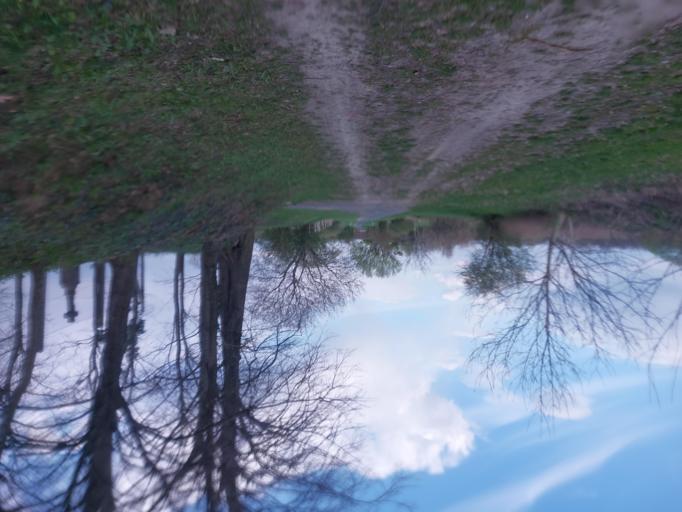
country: HU
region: Veszprem
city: Devecser
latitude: 47.1526
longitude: 17.4096
